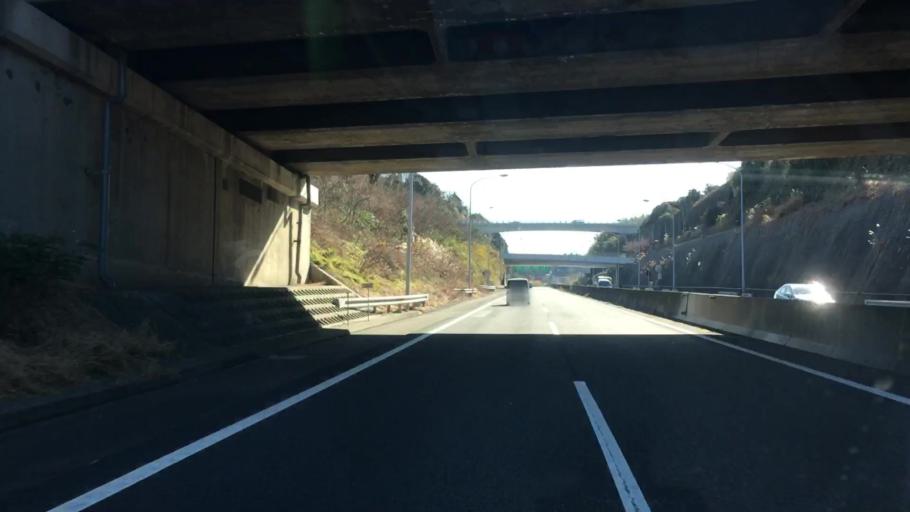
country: JP
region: Kanagawa
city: Kamakura
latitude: 35.3699
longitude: 139.5944
